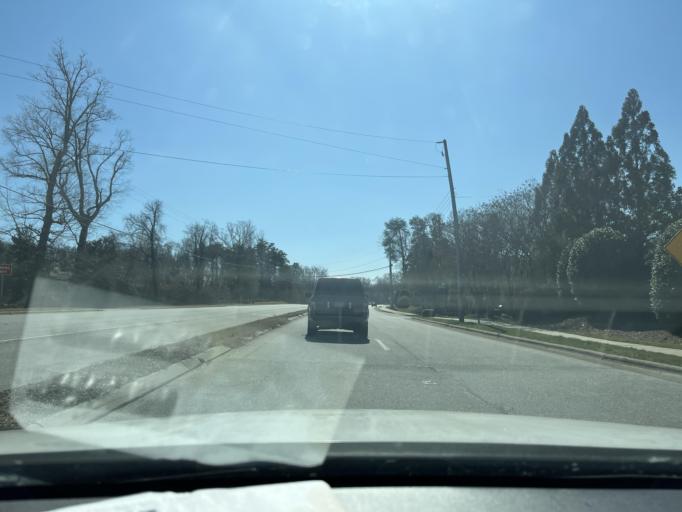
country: US
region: North Carolina
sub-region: Guilford County
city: Jamestown
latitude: 36.0234
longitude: -79.9249
